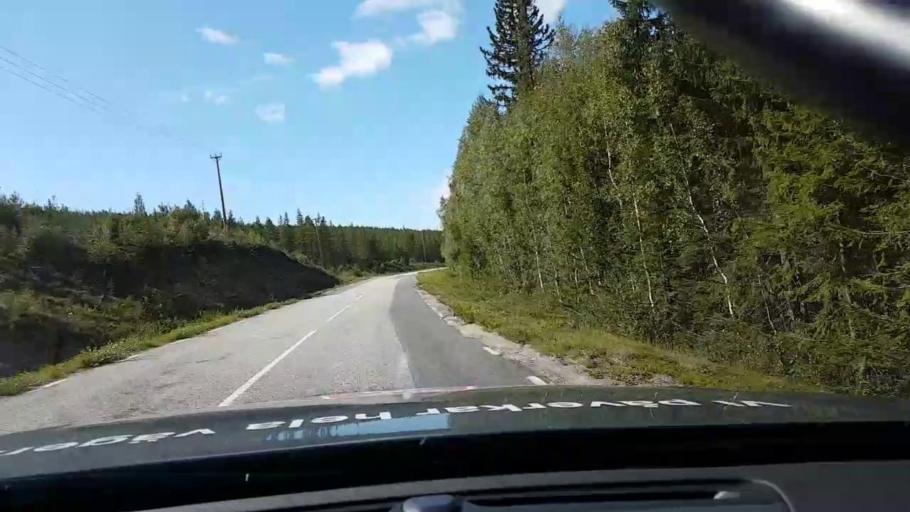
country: SE
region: Vaesterbotten
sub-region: Asele Kommun
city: Asele
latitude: 63.8286
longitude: 17.4649
